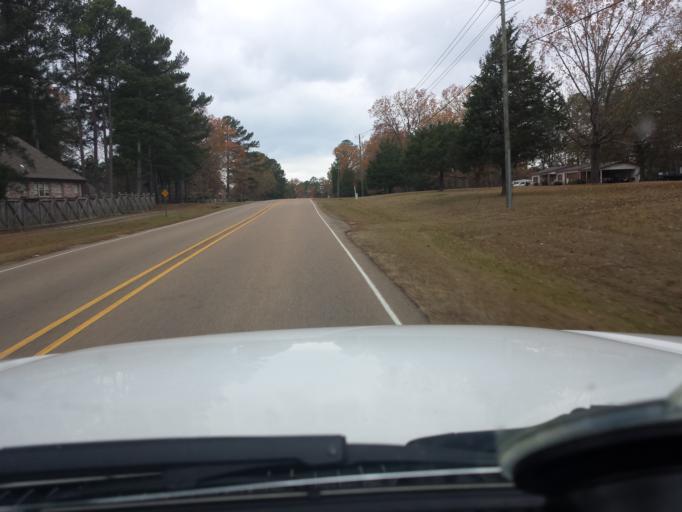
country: US
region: Mississippi
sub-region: Madison County
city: Madison
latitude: 32.4136
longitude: -90.0138
